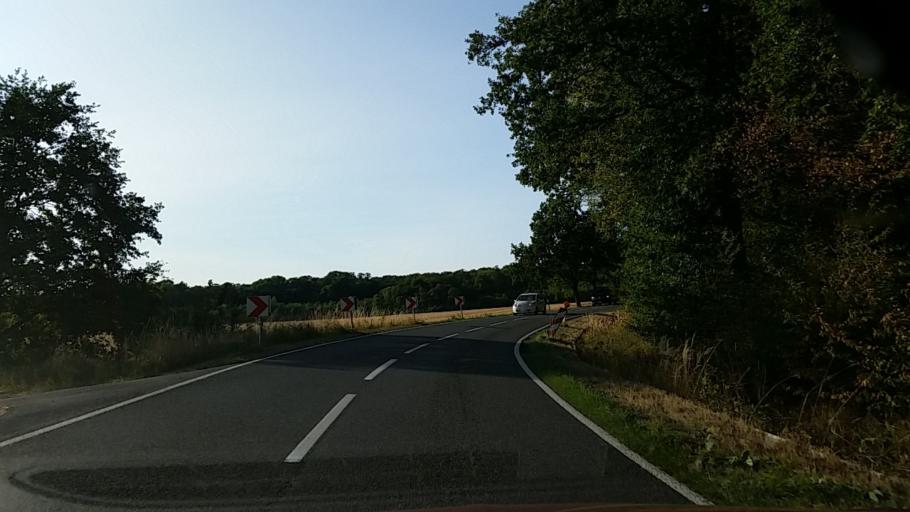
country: DE
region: Lower Saxony
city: Lehre
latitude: 52.3353
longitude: 10.6329
